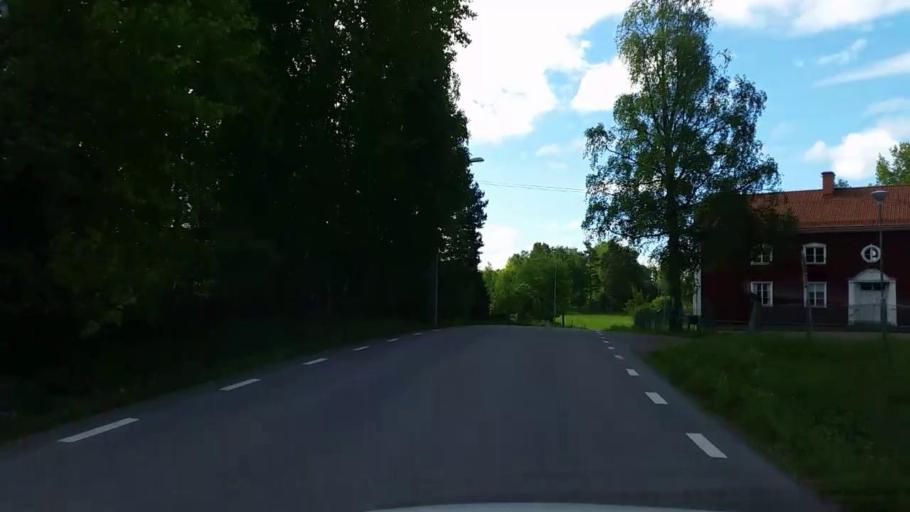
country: SE
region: Dalarna
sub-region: Borlange Kommun
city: Ornas
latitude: 60.5114
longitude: 15.5707
